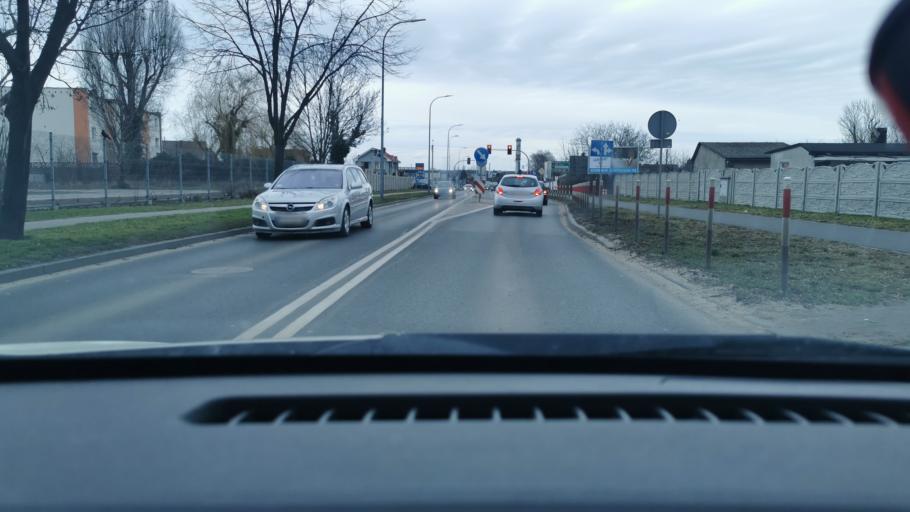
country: PL
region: Greater Poland Voivodeship
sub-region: Powiat ostrowski
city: Ostrow Wielkopolski
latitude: 51.6522
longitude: 17.8383
